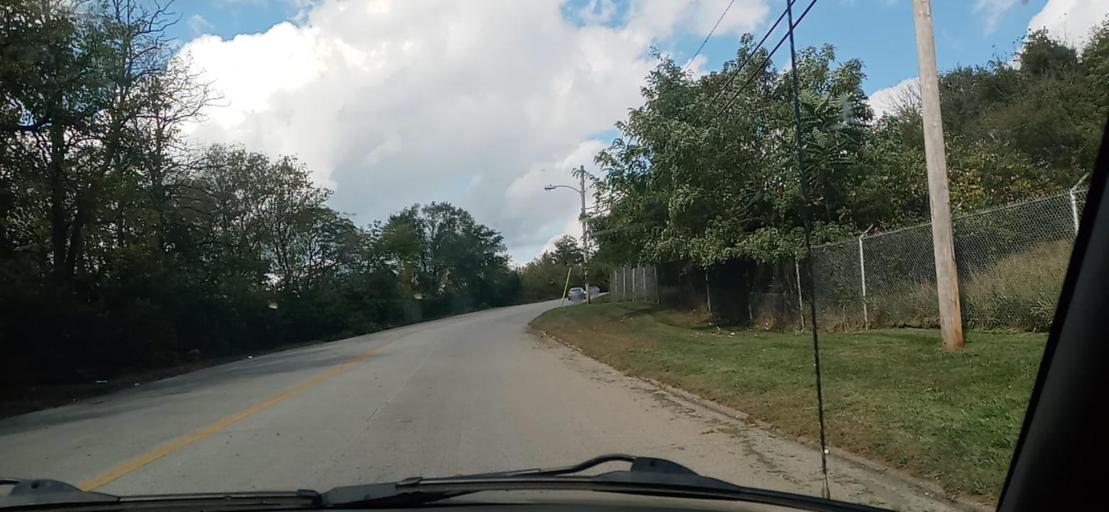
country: US
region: Ohio
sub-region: Summit County
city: Akron
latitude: 41.0889
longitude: -81.4940
